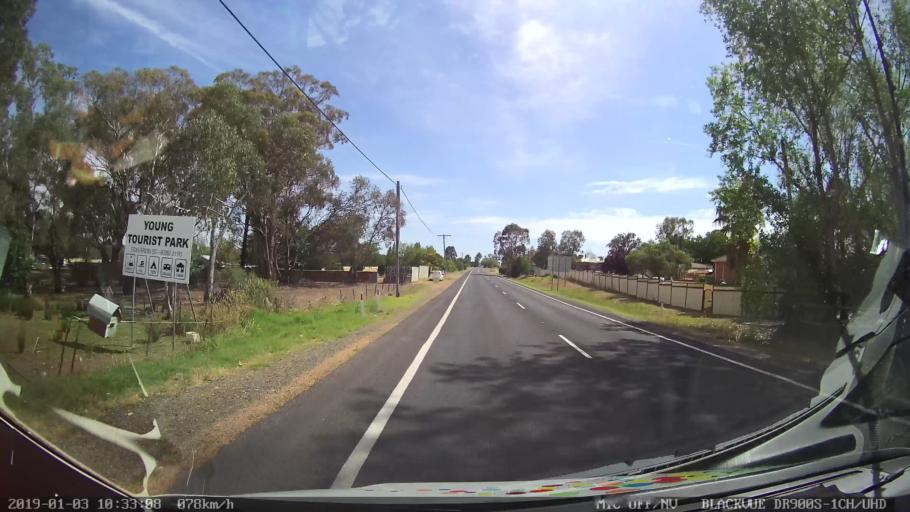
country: AU
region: New South Wales
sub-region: Young
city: Young
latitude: -34.3313
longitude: 148.2858
